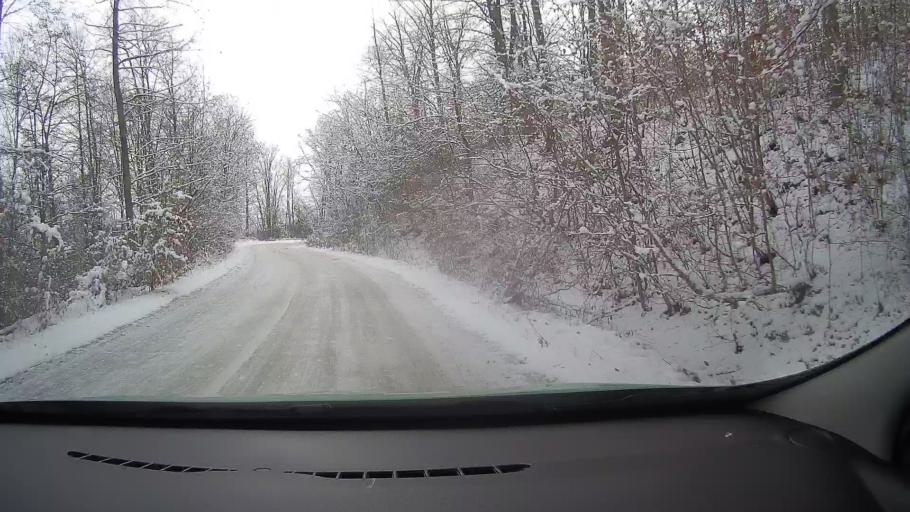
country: RO
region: Alba
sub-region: Comuna Almasu Mare
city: Almasu Mare
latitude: 46.0970
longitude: 23.1713
